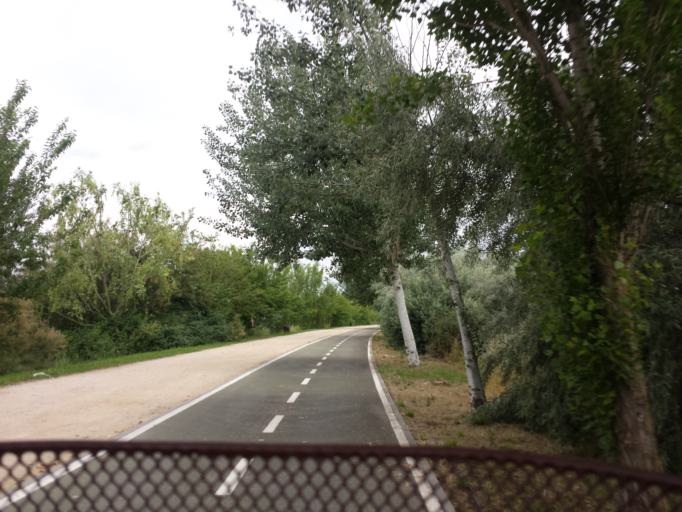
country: ES
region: Aragon
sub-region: Provincia de Zaragoza
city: Almozara
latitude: 41.6778
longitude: -0.9032
